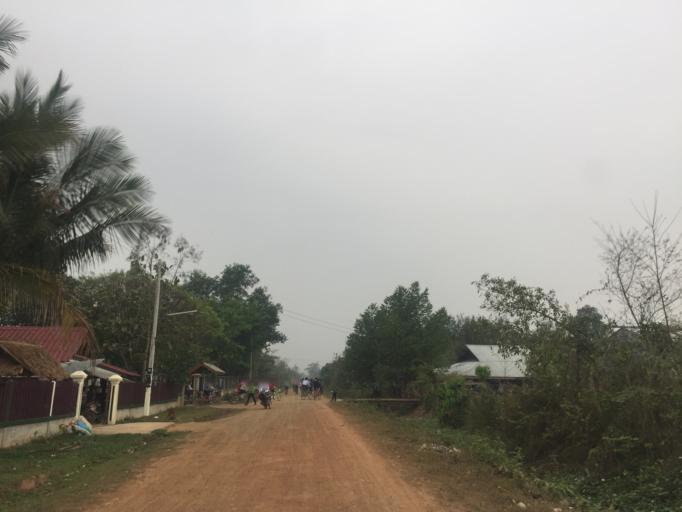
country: LA
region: Xiagnabouli
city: Sainyabuli
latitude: 19.0041
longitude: 101.5150
